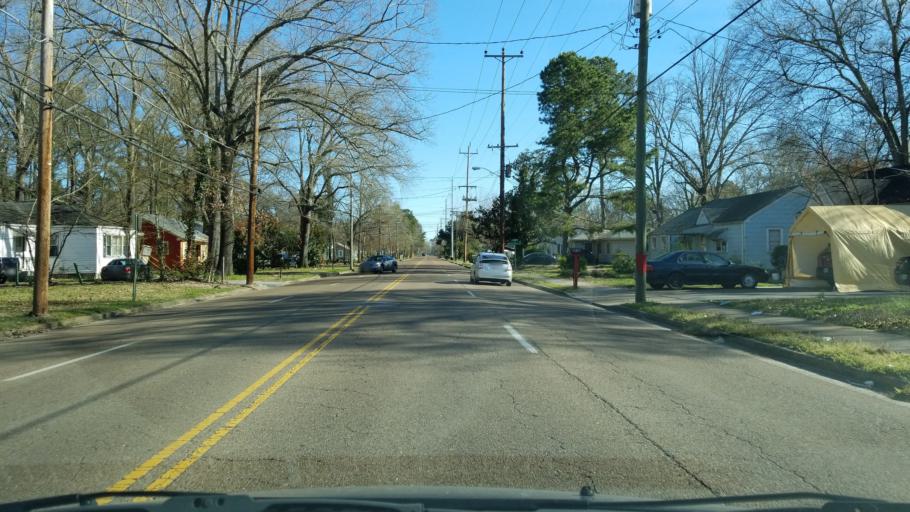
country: US
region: Tennessee
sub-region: Hamilton County
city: East Ridge
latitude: 35.0214
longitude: -85.2236
